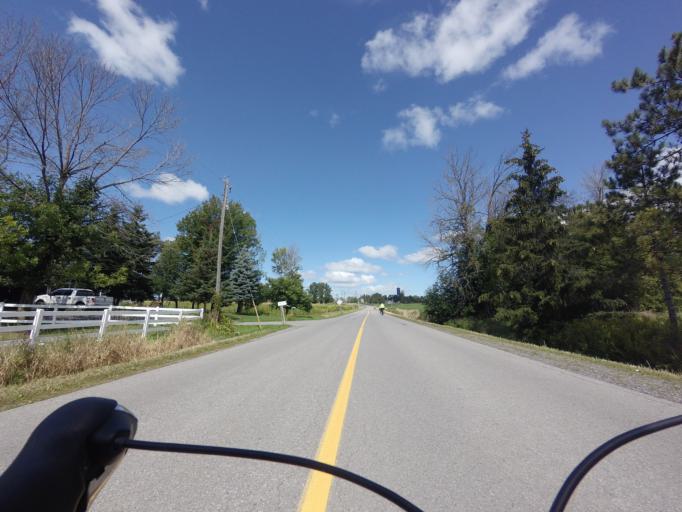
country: CA
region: Ontario
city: Bells Corners
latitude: 45.2562
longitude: -75.8094
